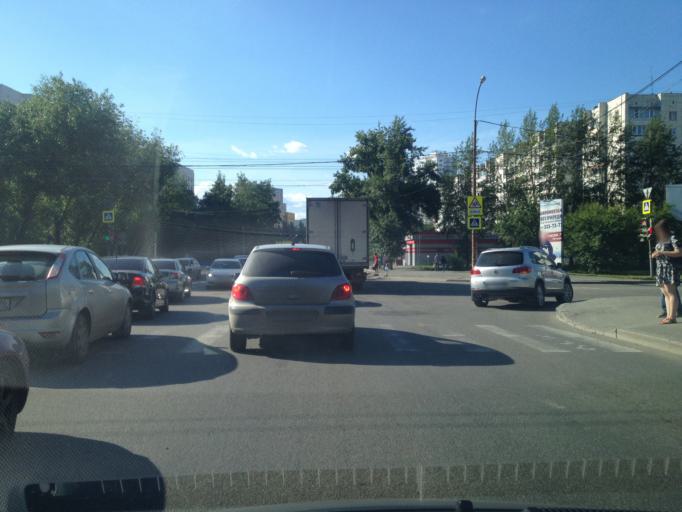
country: RU
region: Sverdlovsk
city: Yekaterinburg
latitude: 56.9023
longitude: 60.6250
